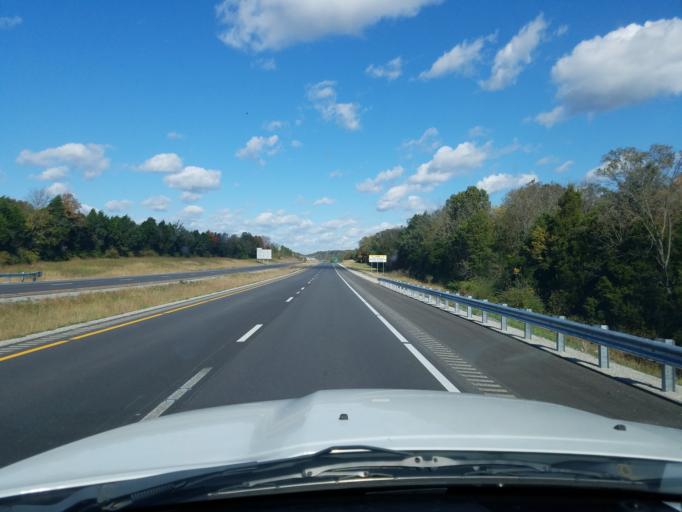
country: US
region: Kentucky
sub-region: Warren County
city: Bowling Green
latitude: 36.9789
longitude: -86.5010
